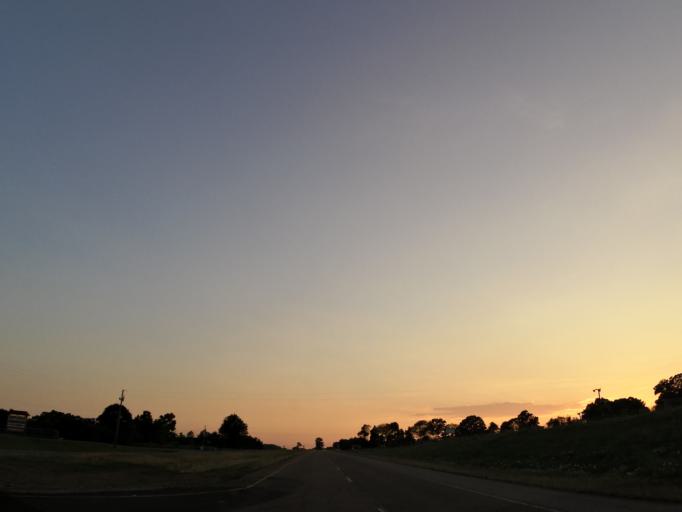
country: US
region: Tennessee
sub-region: Carroll County
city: McKenzie
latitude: 36.1963
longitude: -88.4161
